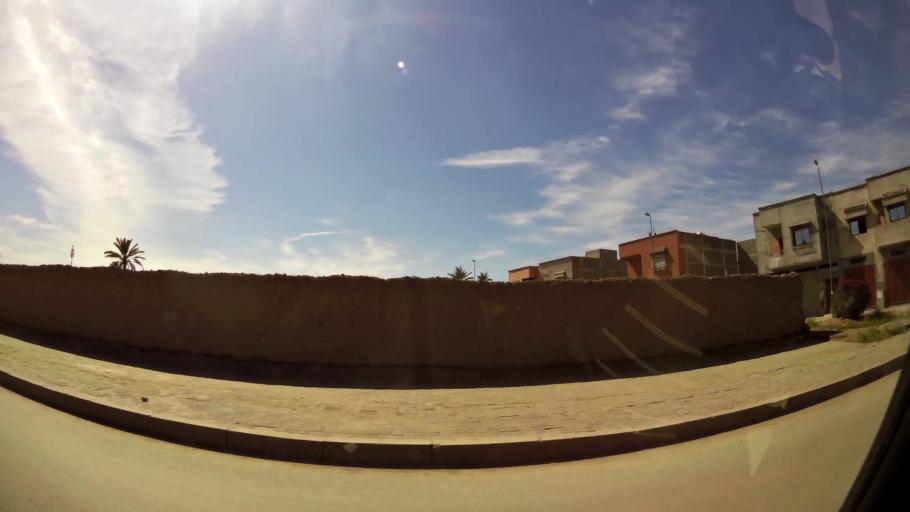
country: MA
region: Marrakech-Tensift-Al Haouz
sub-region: Marrakech
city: Marrakesh
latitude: 31.6227
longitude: -7.9667
